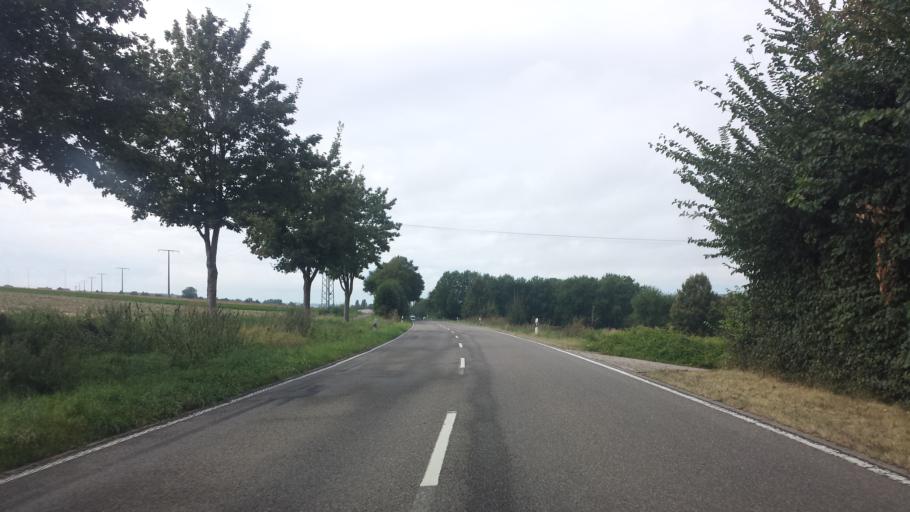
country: DE
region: Rheinland-Pfalz
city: Westhofen
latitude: 49.7053
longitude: 8.2725
